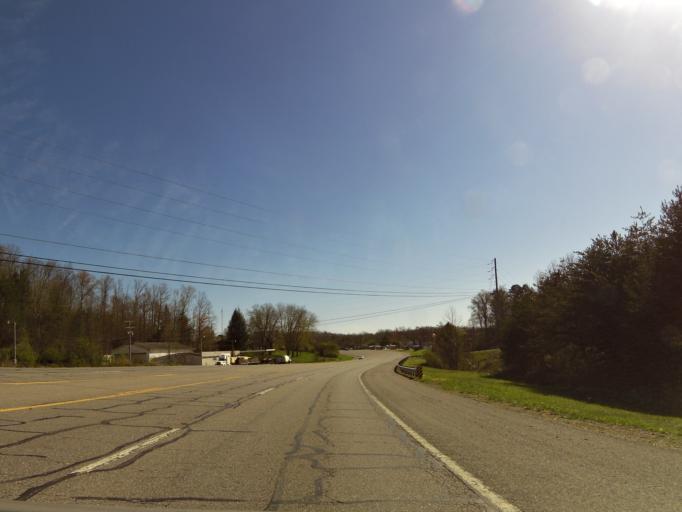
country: US
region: Tennessee
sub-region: Scott County
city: Huntsville
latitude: 36.4223
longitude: -84.5363
